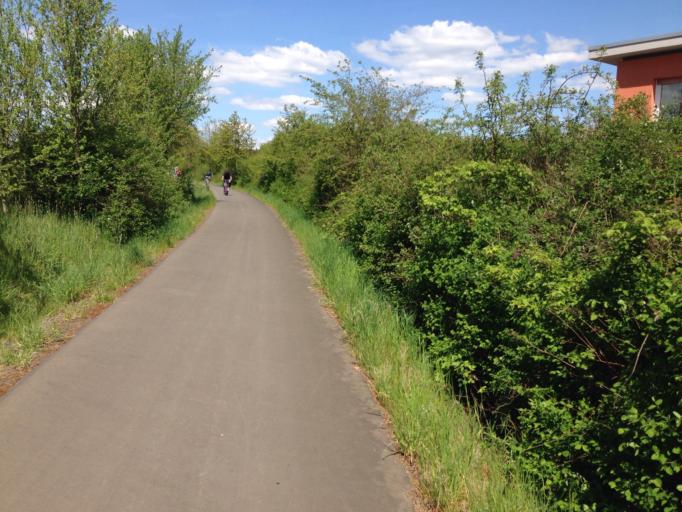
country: DE
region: Hesse
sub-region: Regierungsbezirk Giessen
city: Hungen
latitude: 50.5097
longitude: 8.9321
